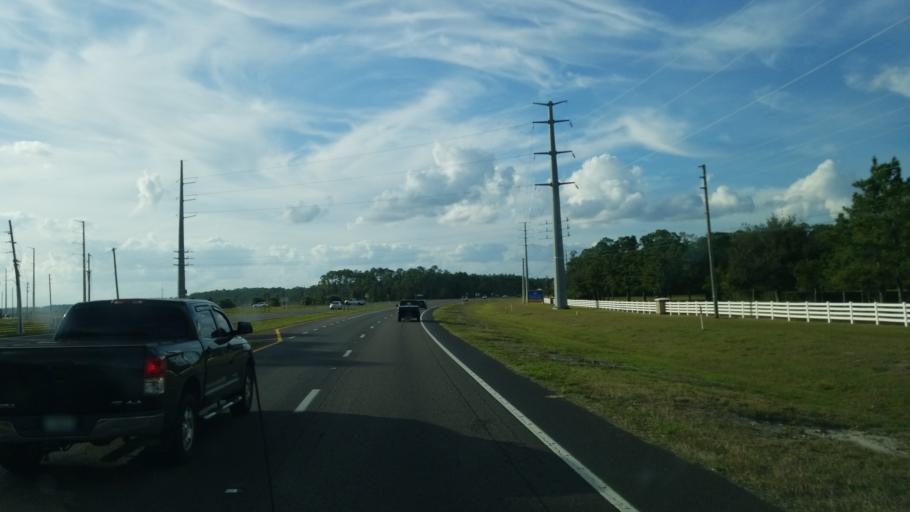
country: US
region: Florida
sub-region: Osceola County
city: Saint Cloud
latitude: 28.1956
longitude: -81.1617
